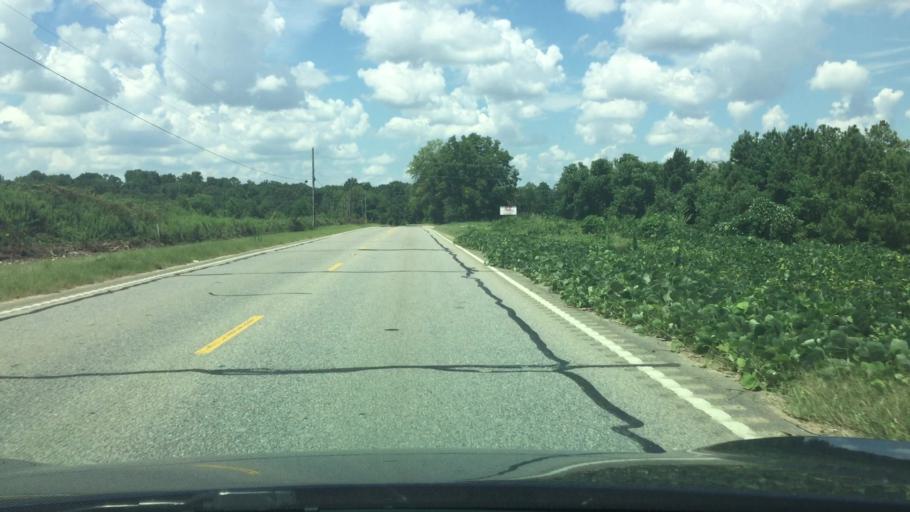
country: US
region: Alabama
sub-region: Montgomery County
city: Pike Road
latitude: 32.3689
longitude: -86.0271
